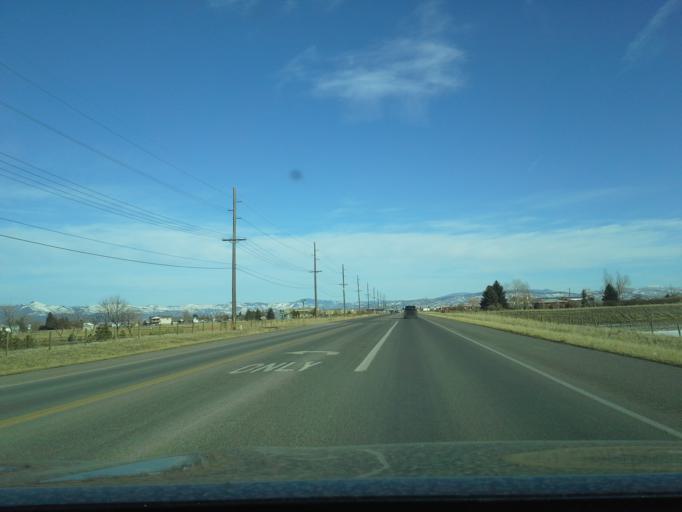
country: US
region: Montana
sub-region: Lewis and Clark County
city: Helena Valley Southeast
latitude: 46.6168
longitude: -111.9505
